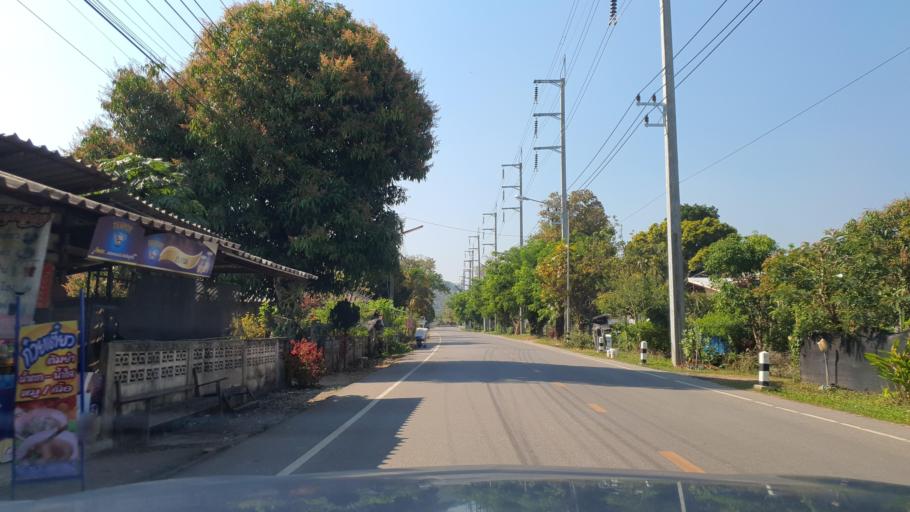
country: TH
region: Chiang Rai
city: Mae Lao
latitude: 19.8050
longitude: 99.6782
